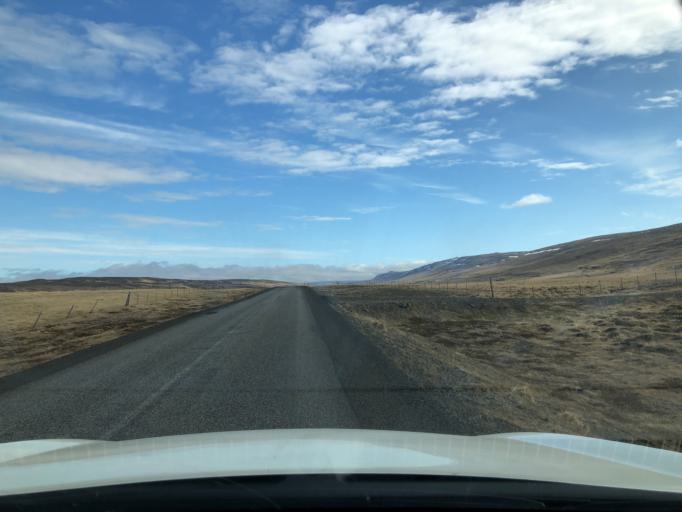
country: IS
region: West
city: Borgarnes
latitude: 65.1113
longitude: -21.6904
